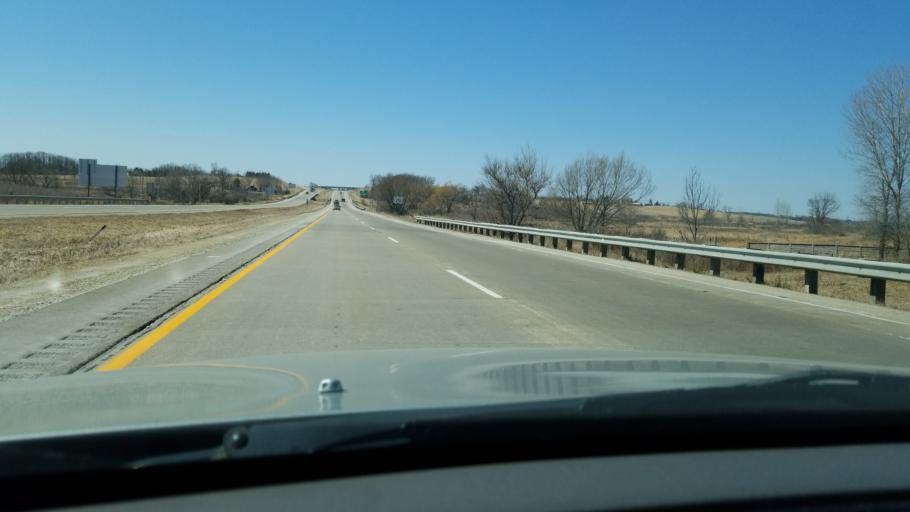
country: US
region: Wisconsin
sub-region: Dane County
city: Verona
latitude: 42.9868
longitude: -89.5675
